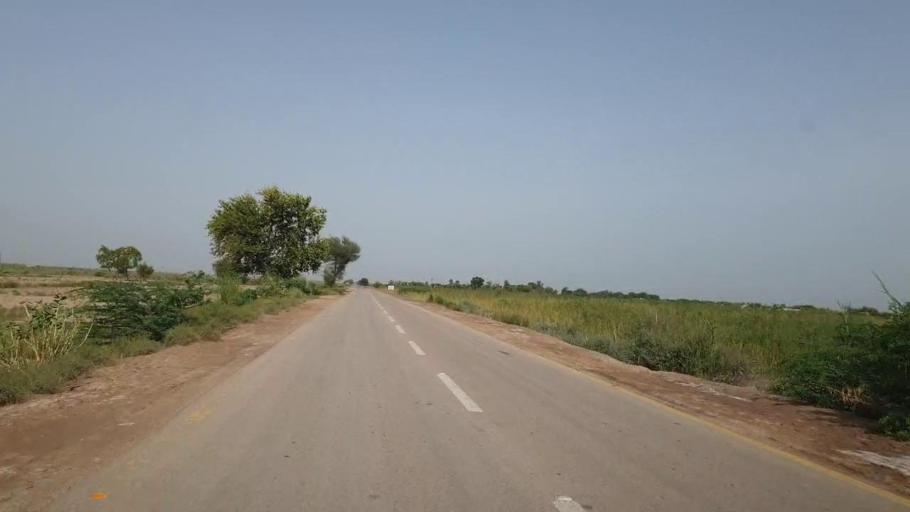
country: PK
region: Sindh
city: Bandhi
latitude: 26.5874
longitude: 68.2325
